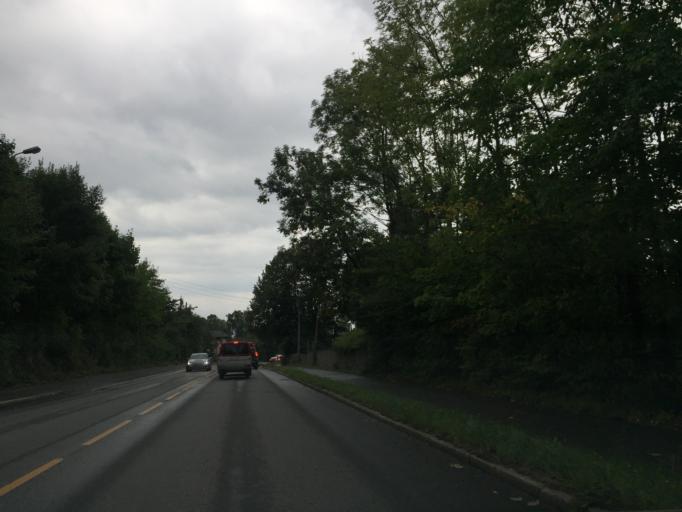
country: NO
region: Oslo
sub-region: Oslo
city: Sjolyststranda
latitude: 59.9434
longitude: 10.6812
